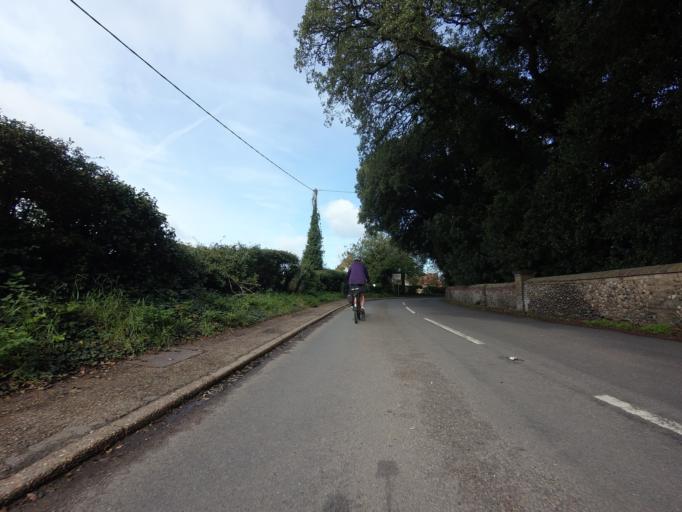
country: GB
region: England
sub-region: Norfolk
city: Wells-next-the-Sea
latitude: 52.9446
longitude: 0.7305
